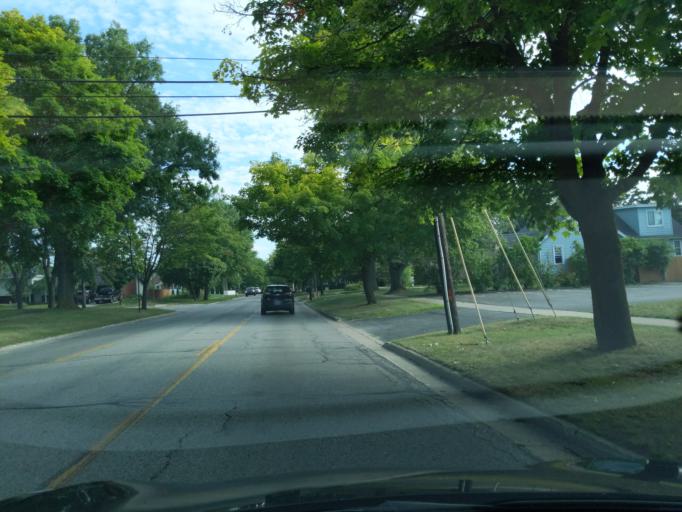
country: US
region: Michigan
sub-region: Midland County
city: Midland
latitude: 43.6459
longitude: -84.2269
